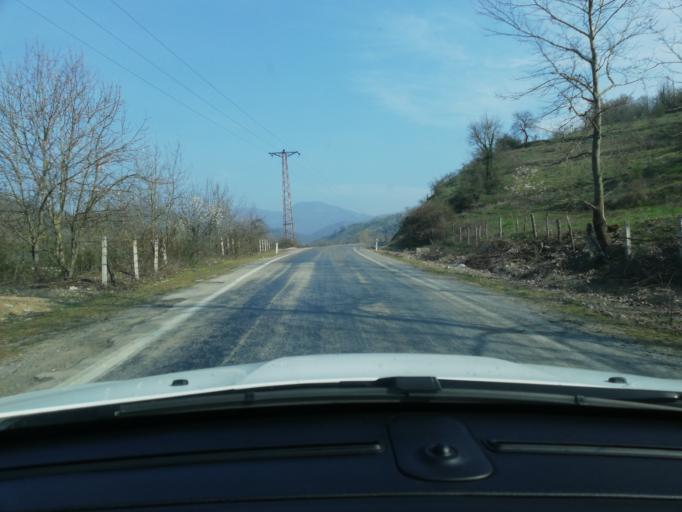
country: TR
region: Karabuk
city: Yenice
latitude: 41.2311
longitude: 32.3605
